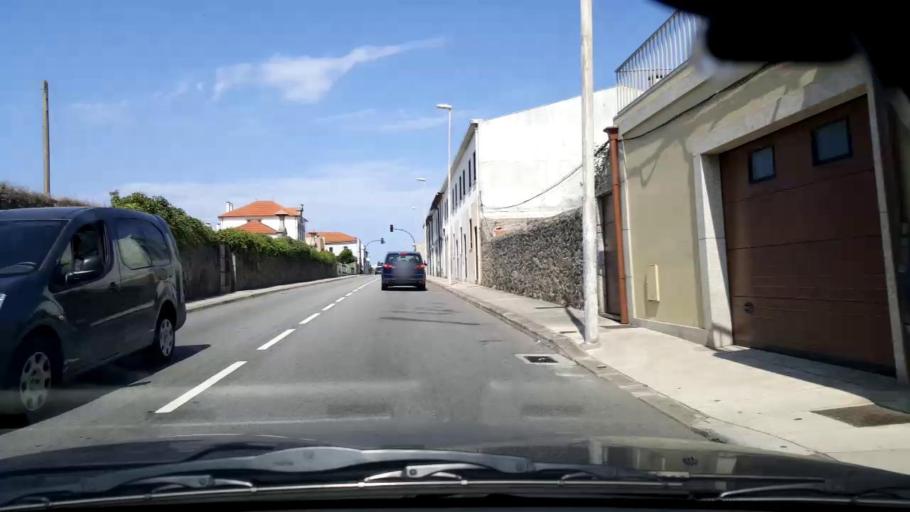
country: PT
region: Porto
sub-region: Vila do Conde
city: Vila do Conde
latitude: 41.3577
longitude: -8.7425
